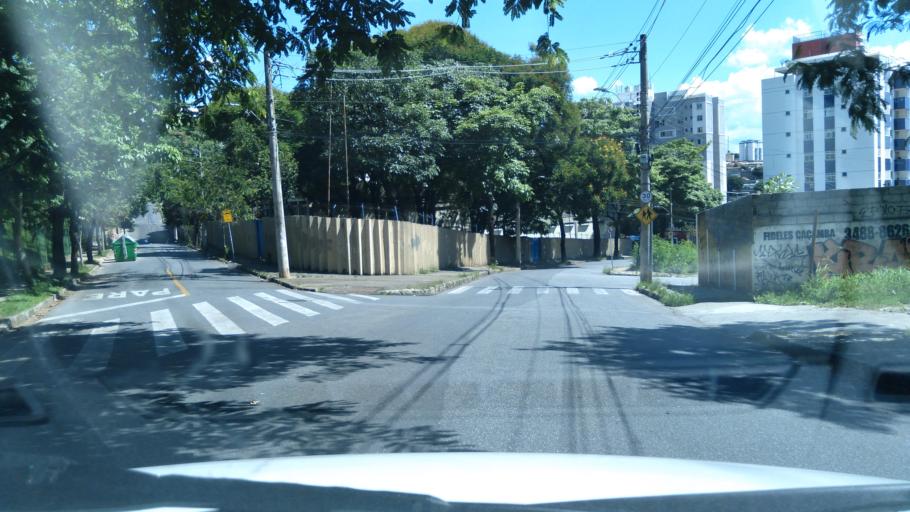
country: BR
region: Minas Gerais
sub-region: Belo Horizonte
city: Belo Horizonte
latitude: -19.8733
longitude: -43.9145
